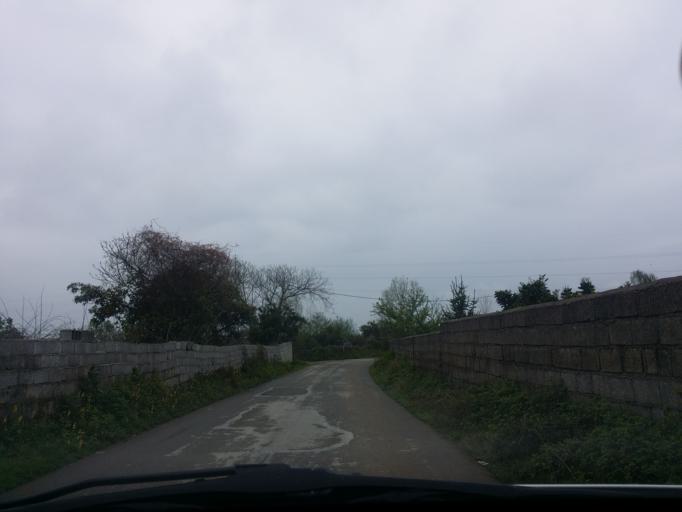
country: IR
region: Mazandaran
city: Chalus
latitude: 36.6731
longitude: 51.3791
